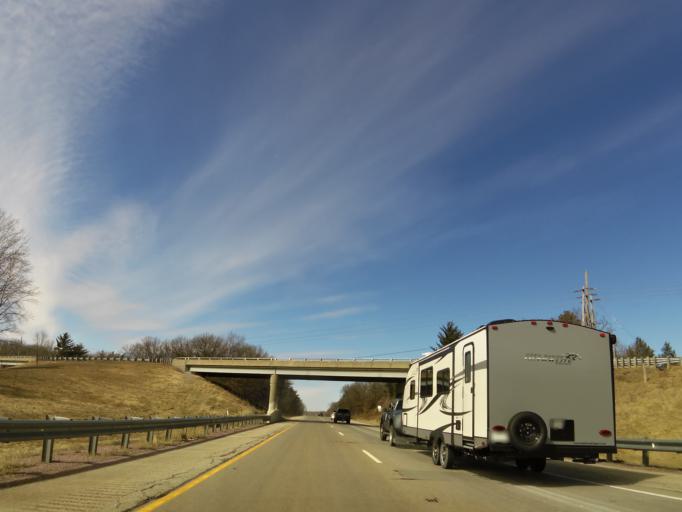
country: US
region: Wisconsin
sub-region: Juneau County
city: New Lisbon
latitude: 43.8617
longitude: -90.1152
